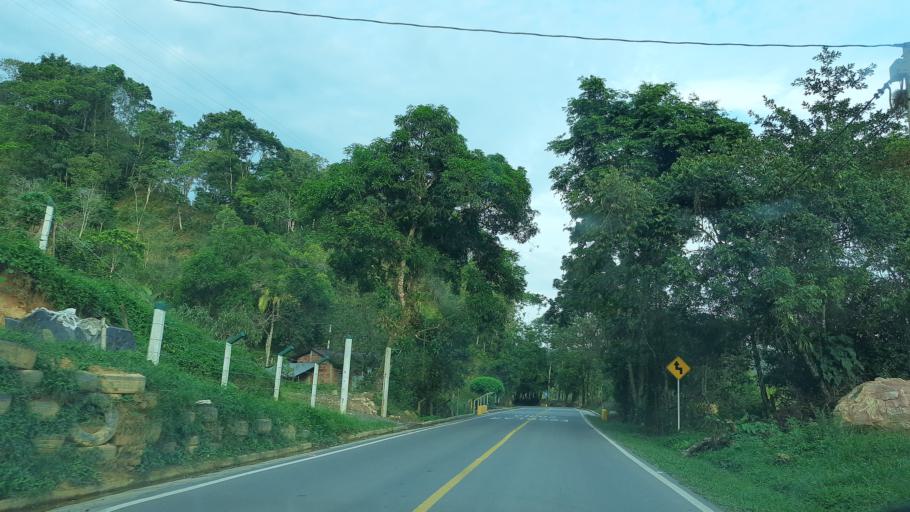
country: CO
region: Boyaca
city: San Luis de Gaceno
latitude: 4.8167
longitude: -73.1817
